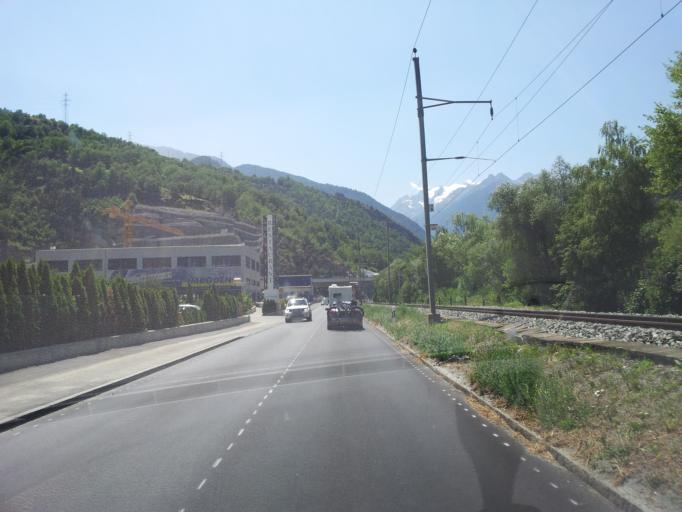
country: CH
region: Valais
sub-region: Visp District
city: Visp
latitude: 46.2802
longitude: 7.8822
